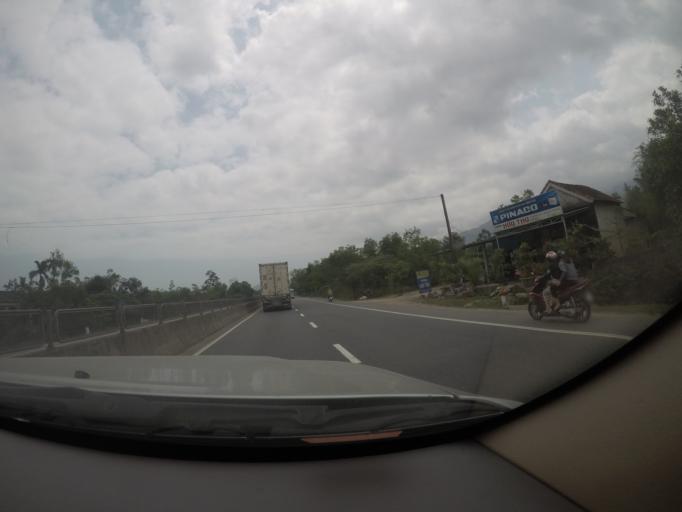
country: VN
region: Thua Thien-Hue
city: Phu Loc
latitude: 16.2720
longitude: 107.9679
